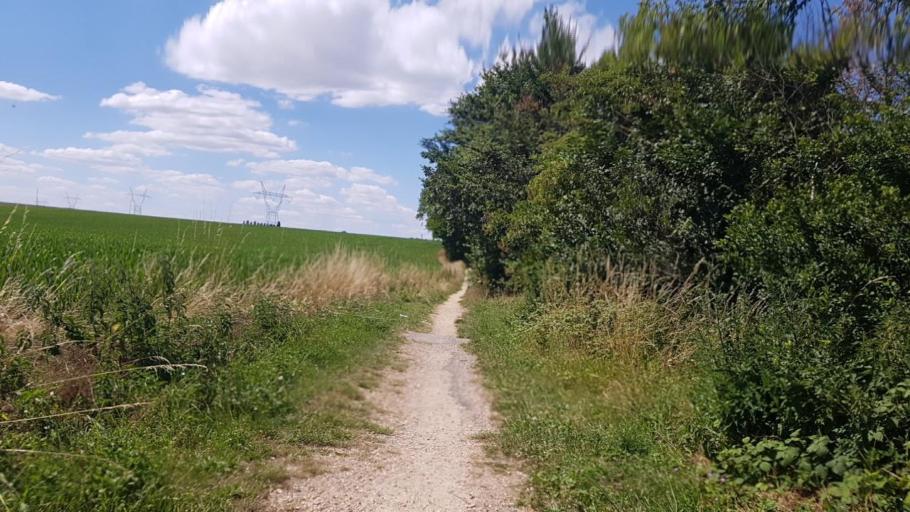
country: FR
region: Ile-de-France
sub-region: Departement de Seine-et-Marne
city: Moussy-le-Vieux
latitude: 49.0384
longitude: 2.6356
